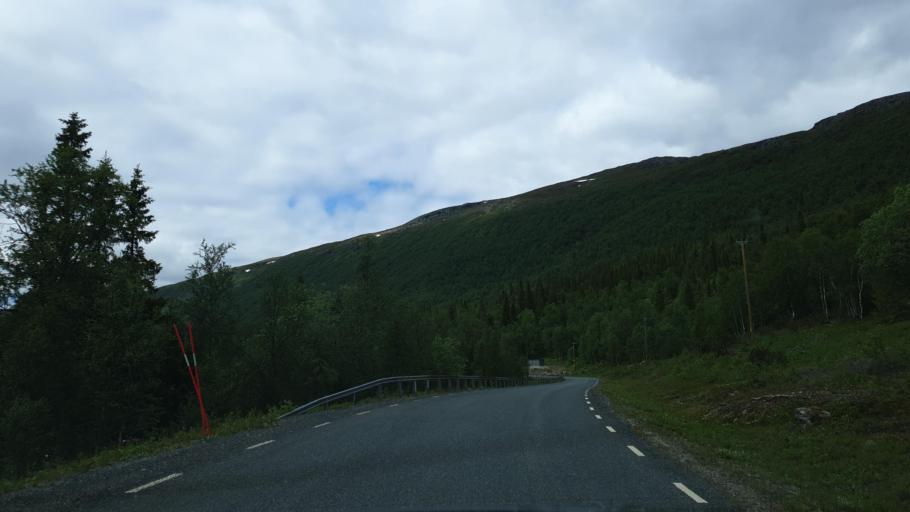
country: NO
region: Nordland
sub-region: Hattfjelldal
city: Hattfjelldal
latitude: 65.4266
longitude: 14.6013
